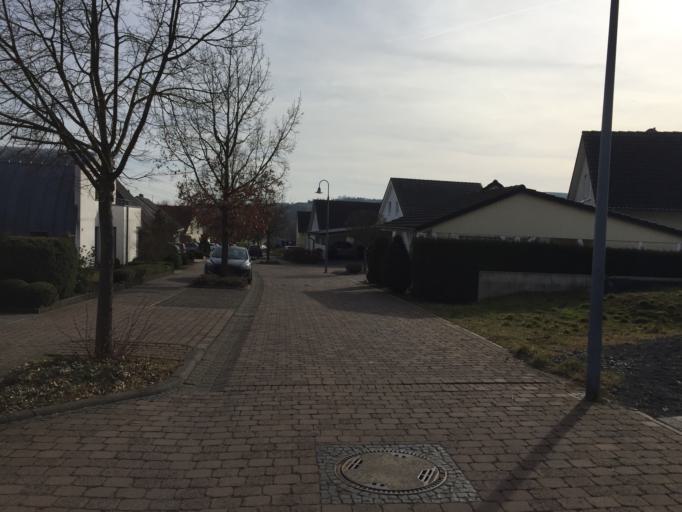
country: DE
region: Hesse
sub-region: Regierungsbezirk Giessen
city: Fronhausen
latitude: 50.6836
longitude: 8.6921
